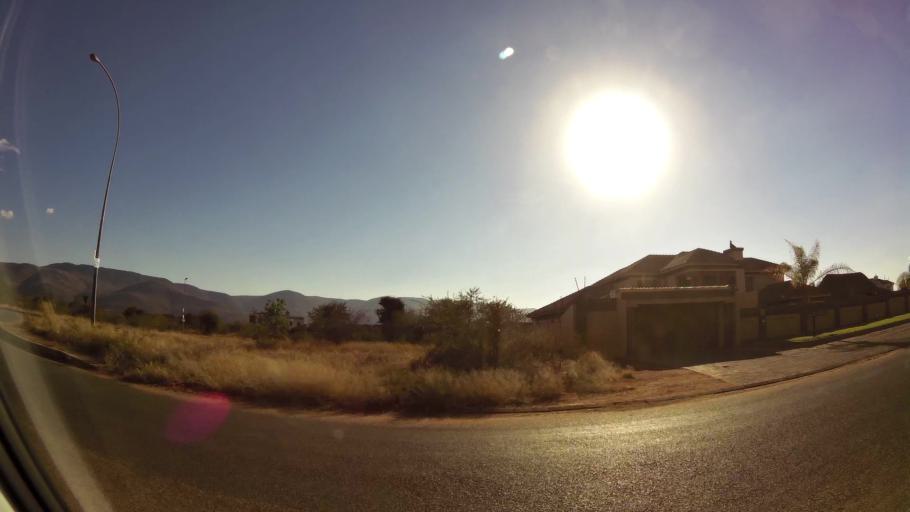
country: ZA
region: Limpopo
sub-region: Waterberg District Municipality
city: Mokopane
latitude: -24.2028
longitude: 29.0014
